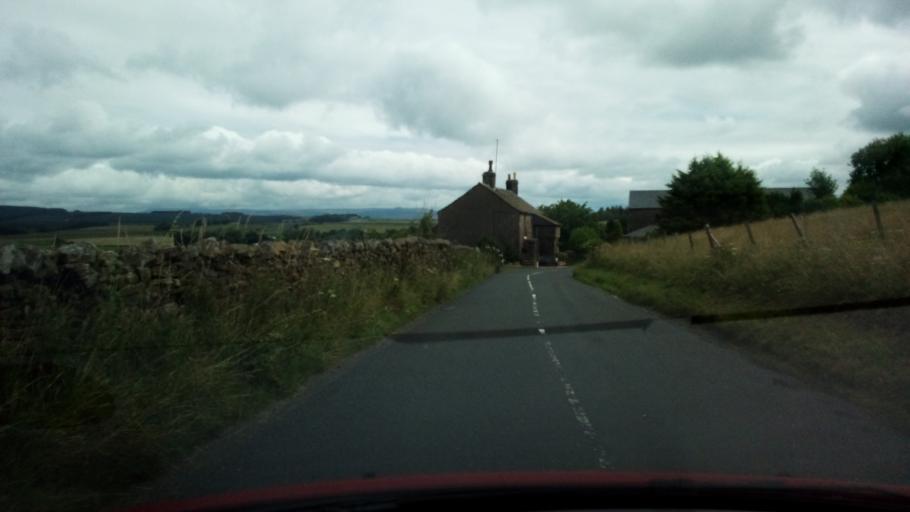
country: GB
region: England
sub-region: Lancashire
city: Clitheroe
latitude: 53.9796
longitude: -2.3913
